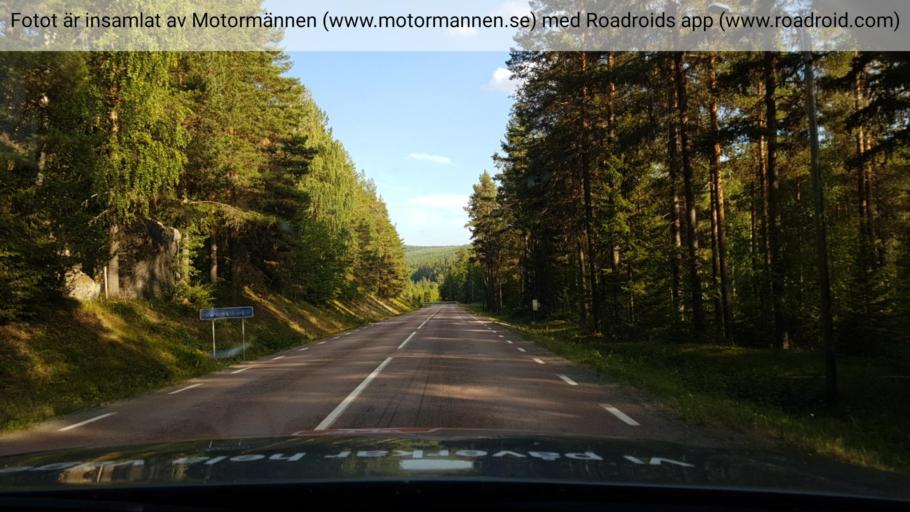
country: SE
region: Vaesternorrland
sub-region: Solleftea Kommun
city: As
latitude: 63.5848
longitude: 16.3355
